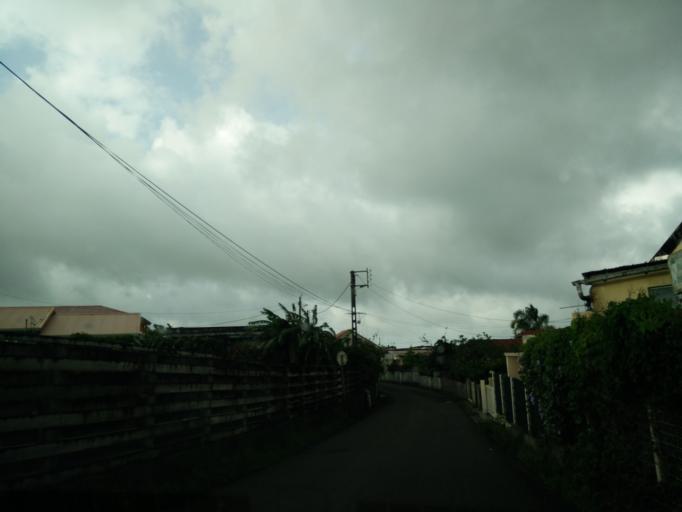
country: MQ
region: Martinique
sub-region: Martinique
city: Le Morne-Rouge
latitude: 14.7741
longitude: -61.1339
